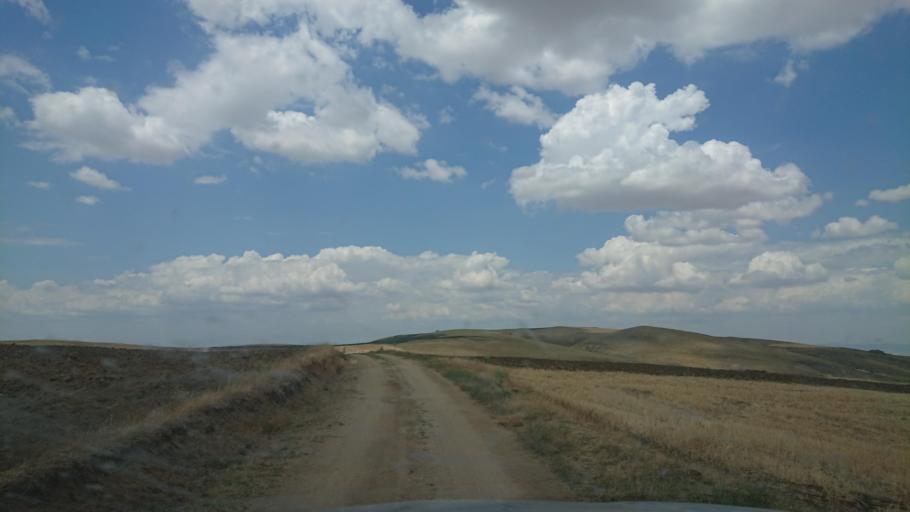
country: TR
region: Aksaray
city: Agacoren
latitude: 38.8982
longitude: 33.8829
